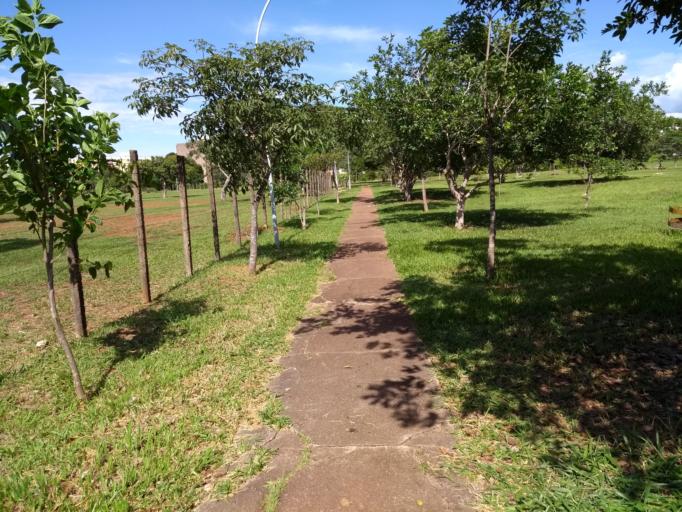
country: BR
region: Federal District
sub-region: Brasilia
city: Brasilia
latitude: -15.8050
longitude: -47.9414
